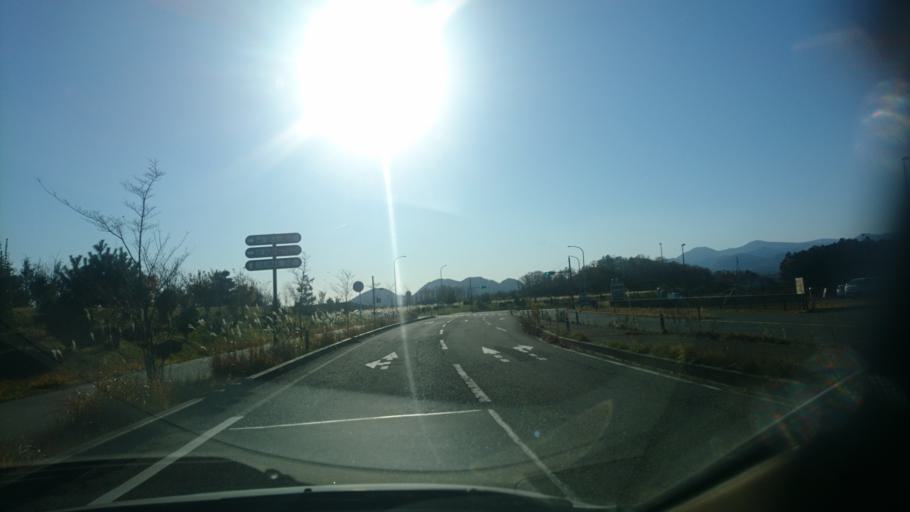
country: JP
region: Miyagi
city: Tomiya
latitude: 38.4690
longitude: 140.8907
